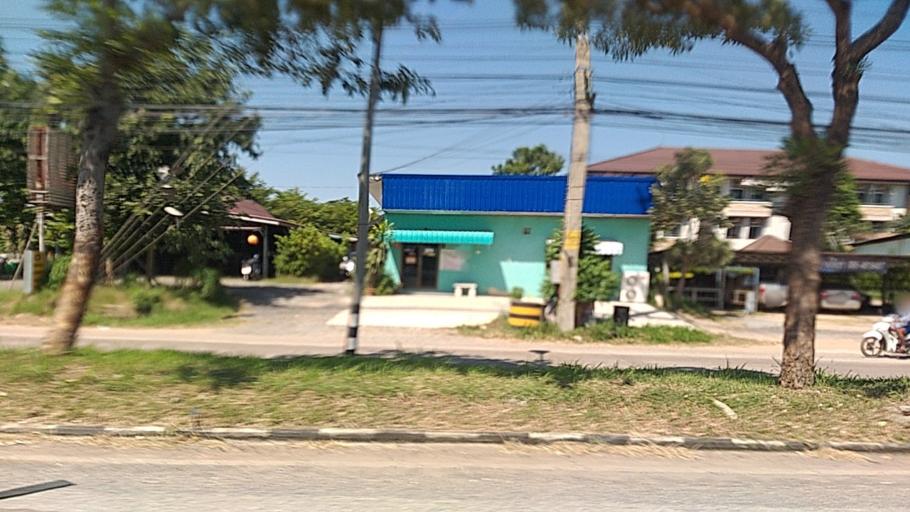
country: TH
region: Nakhon Ratchasima
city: Kham Thale So
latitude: 14.9249
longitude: 101.9610
